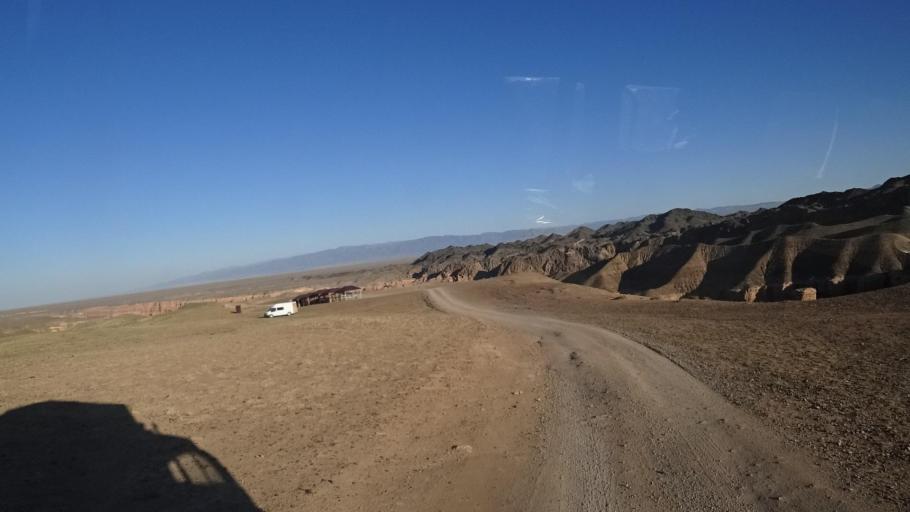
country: KZ
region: Almaty Oblysy
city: Kegen
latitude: 43.3554
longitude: 79.0603
